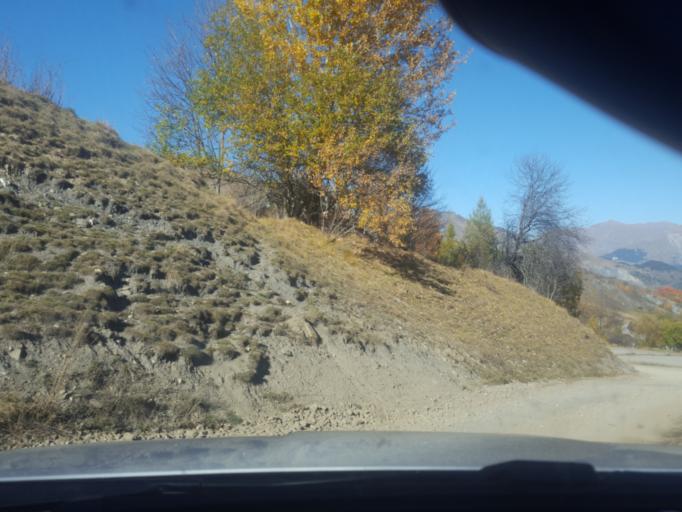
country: FR
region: Rhone-Alpes
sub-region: Departement de la Savoie
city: Saint-Jean-de-Maurienne
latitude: 45.2415
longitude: 6.2658
